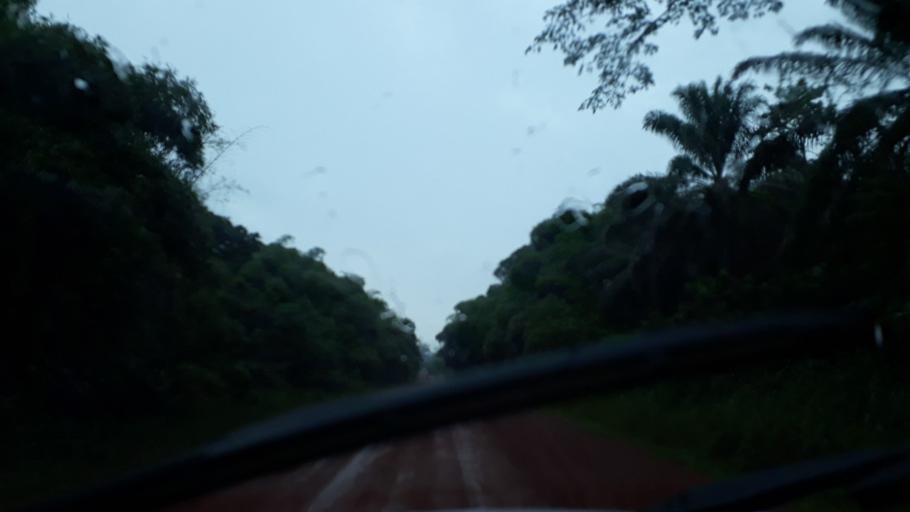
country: CD
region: Eastern Province
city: Kisangani
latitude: 0.4752
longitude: 25.4998
